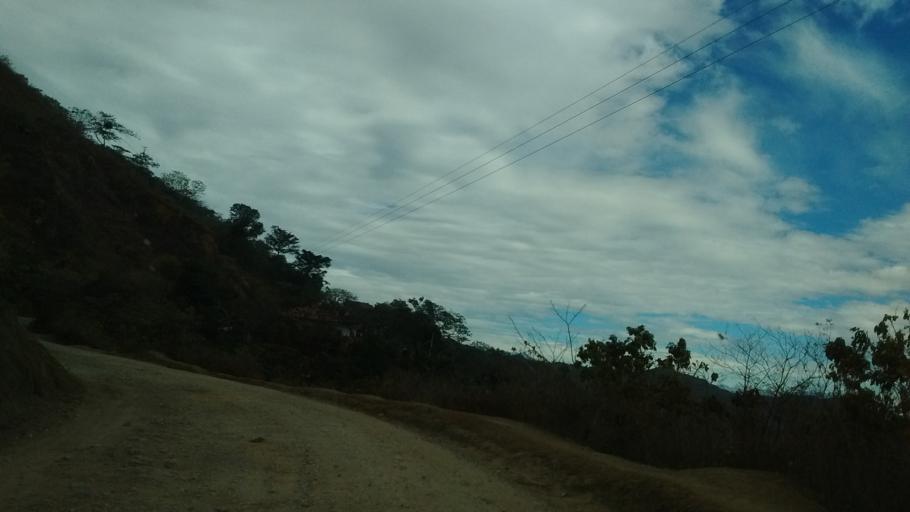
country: CO
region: Cauca
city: Almaguer
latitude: 1.8470
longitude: -76.9000
